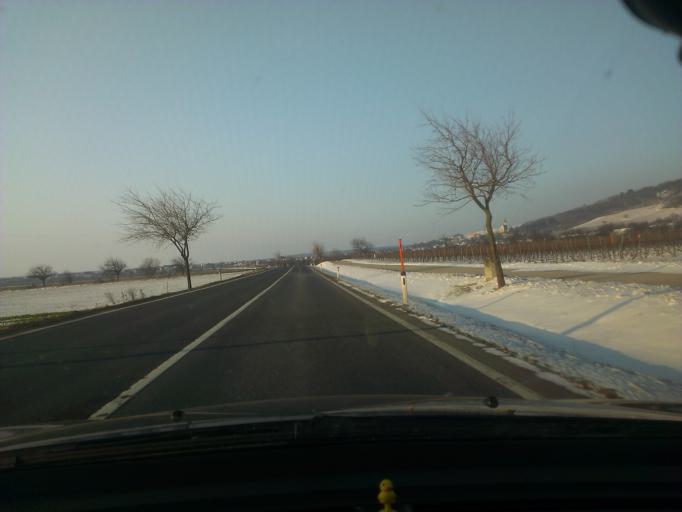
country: AT
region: Burgenland
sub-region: Eisenstadt-Umgebung
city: Donnerskirchen
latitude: 47.9035
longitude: 16.6574
